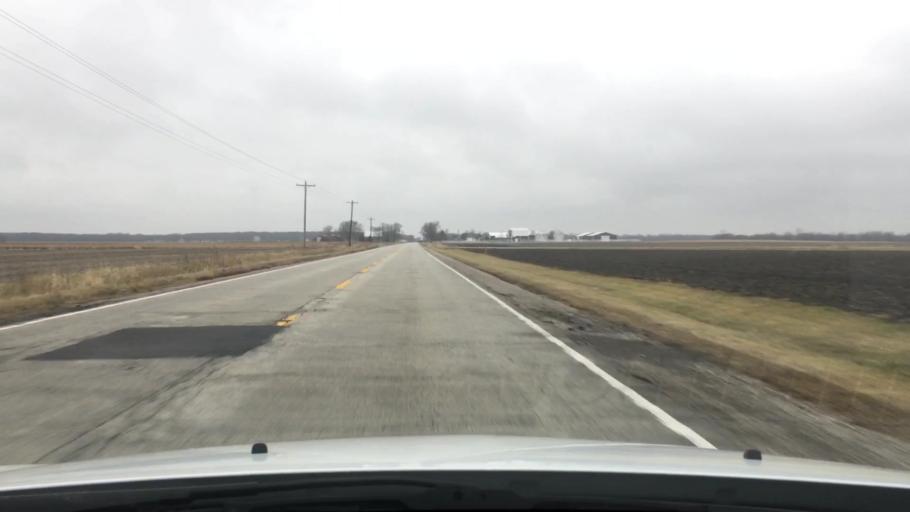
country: US
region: Illinois
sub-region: Iroquois County
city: Watseka
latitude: 40.8866
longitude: -87.8024
